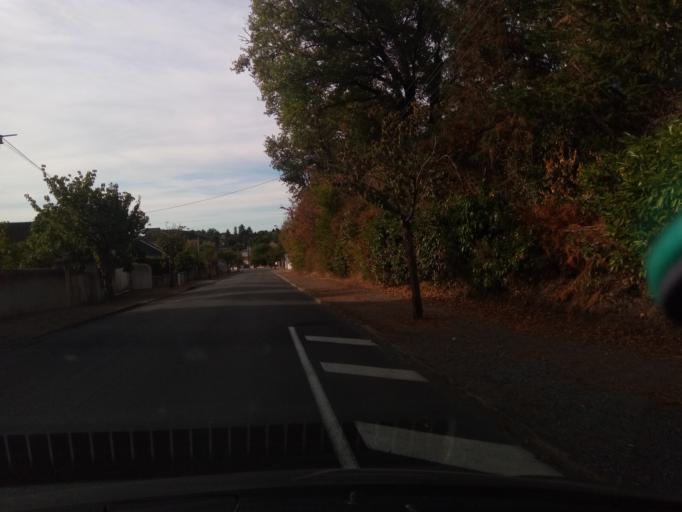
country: FR
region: Poitou-Charentes
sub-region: Departement de la Vienne
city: Montmorillon
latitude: 46.4174
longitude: 0.8805
